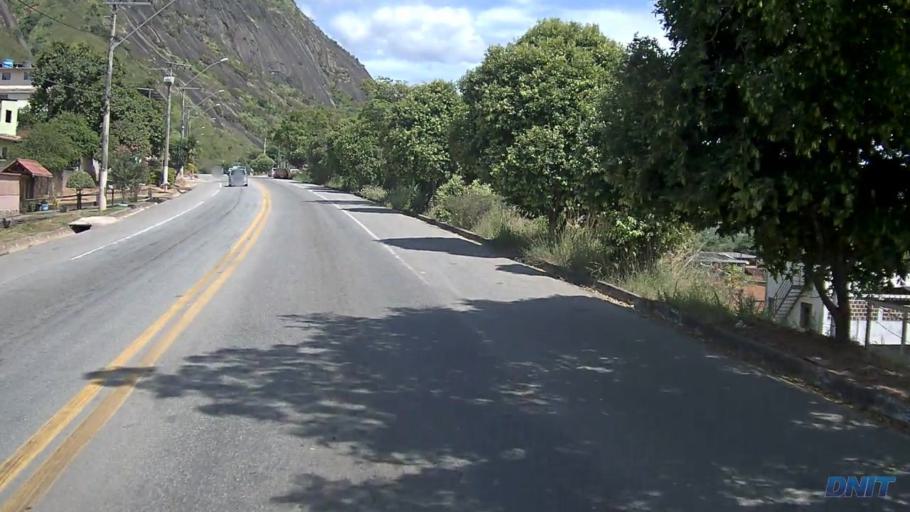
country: BR
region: Minas Gerais
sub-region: Coronel Fabriciano
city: Coronel Fabriciano
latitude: -19.5383
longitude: -42.6707
